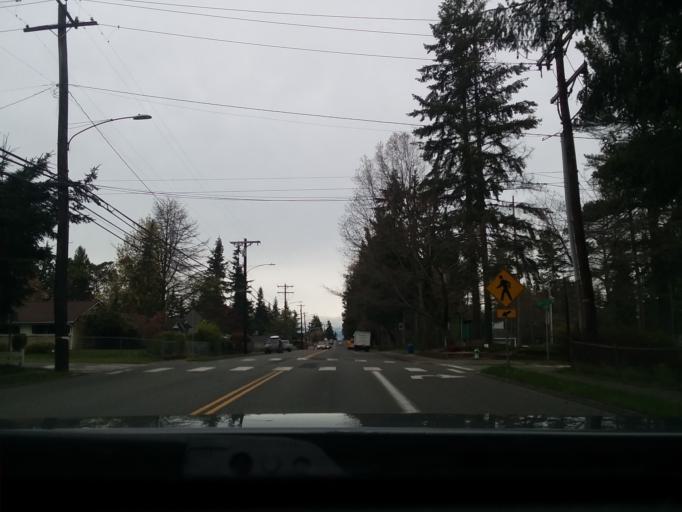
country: US
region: Washington
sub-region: Snohomish County
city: Mountlake Terrace
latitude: 47.7955
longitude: -122.3085
